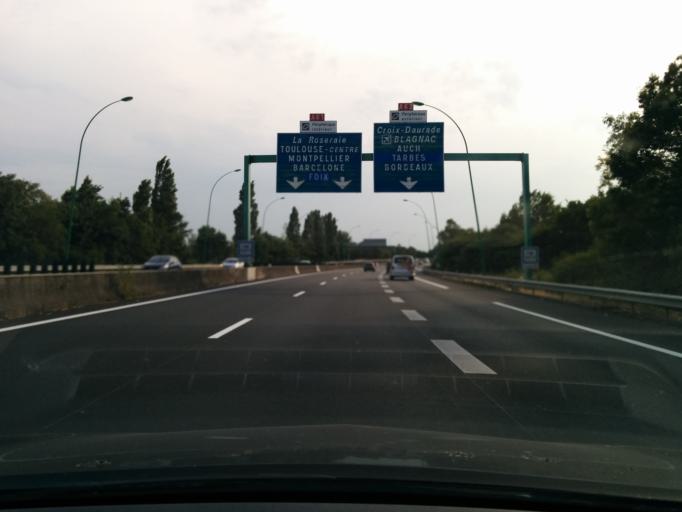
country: FR
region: Midi-Pyrenees
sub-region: Departement de la Haute-Garonne
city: L'Union
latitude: 43.6388
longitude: 1.4852
